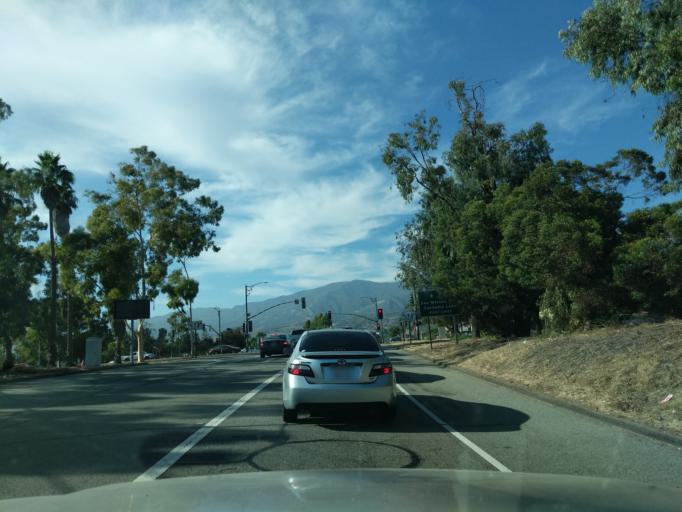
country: US
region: California
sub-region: Santa Barbara County
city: Mission Canyon
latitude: 34.4395
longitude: -119.7539
